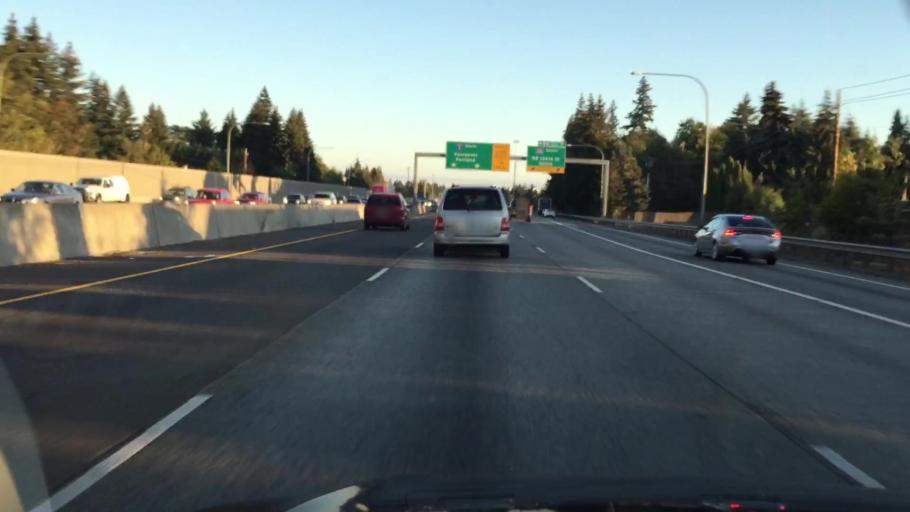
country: US
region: Washington
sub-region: Clark County
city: Salmon Creek
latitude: 45.7307
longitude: -122.6567
